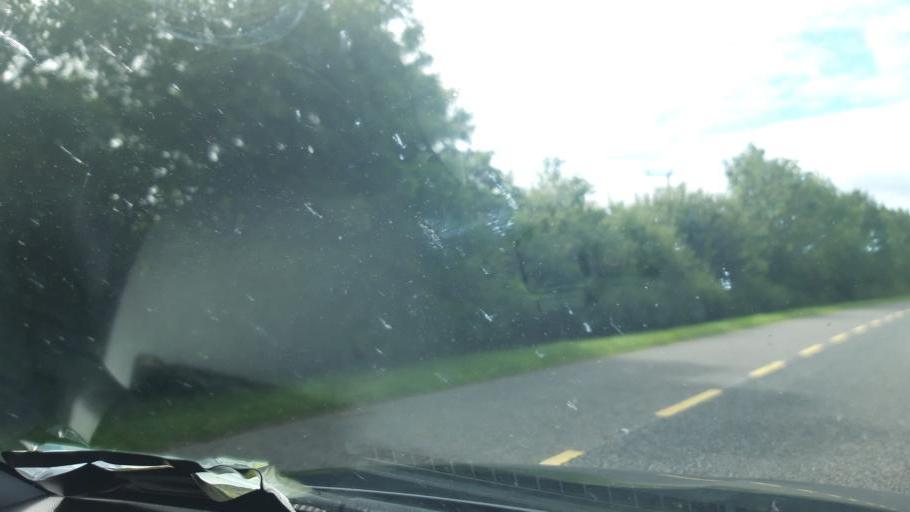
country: IE
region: Leinster
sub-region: Kilkenny
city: Callan
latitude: 52.5350
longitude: -7.3996
